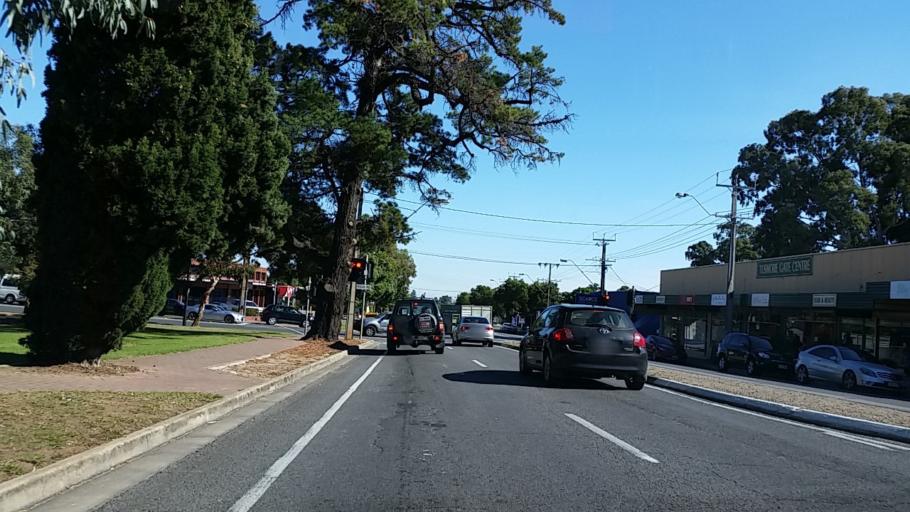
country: AU
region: South Australia
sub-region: Burnside
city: Tusmore
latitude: -34.9388
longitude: 138.6520
